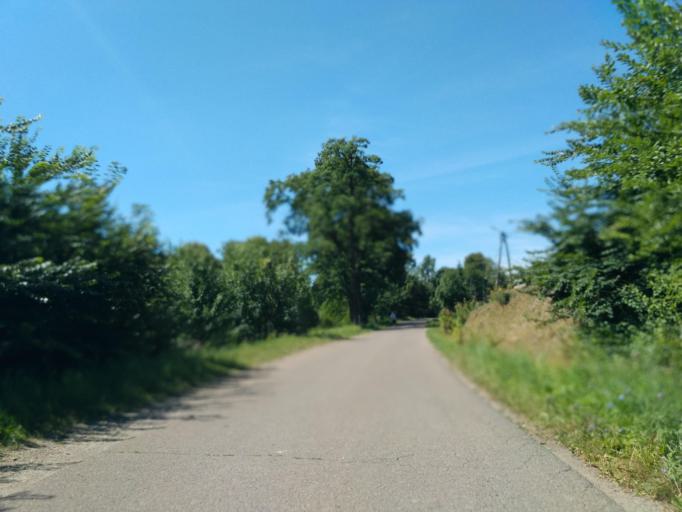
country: PL
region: Subcarpathian Voivodeship
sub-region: Powiat sanocki
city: Nowosielce-Gniewosz
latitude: 49.5382
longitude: 22.0558
